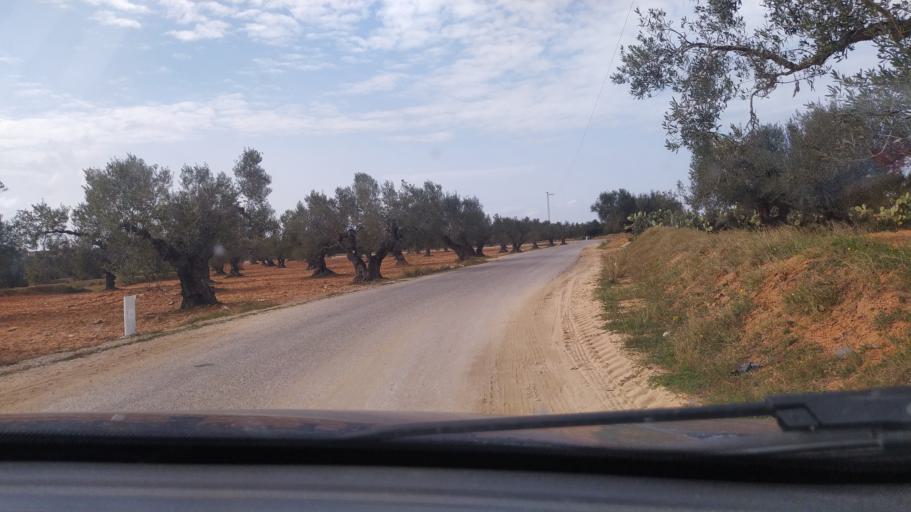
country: TN
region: Al Munastir
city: Sidi Bin Nur
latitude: 35.5261
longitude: 10.9680
